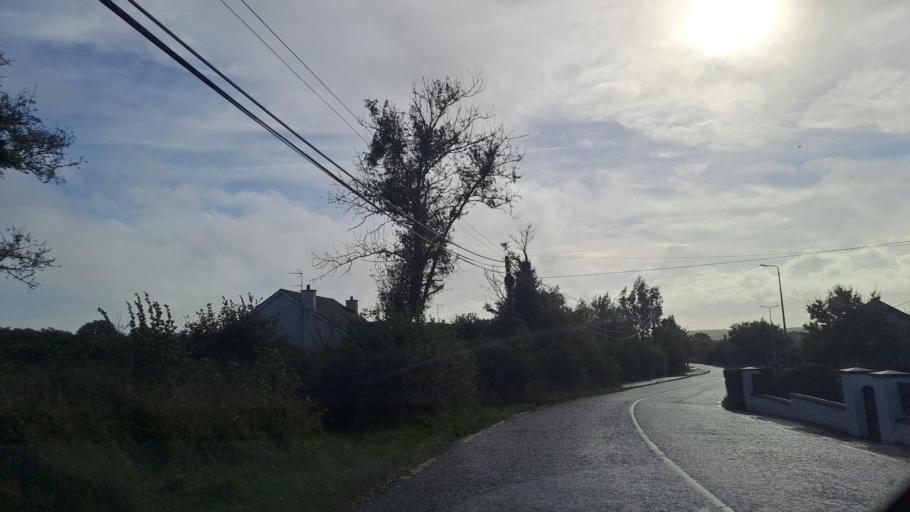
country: IE
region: Ulster
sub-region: County Monaghan
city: Carrickmacross
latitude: 53.9354
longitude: -6.7165
